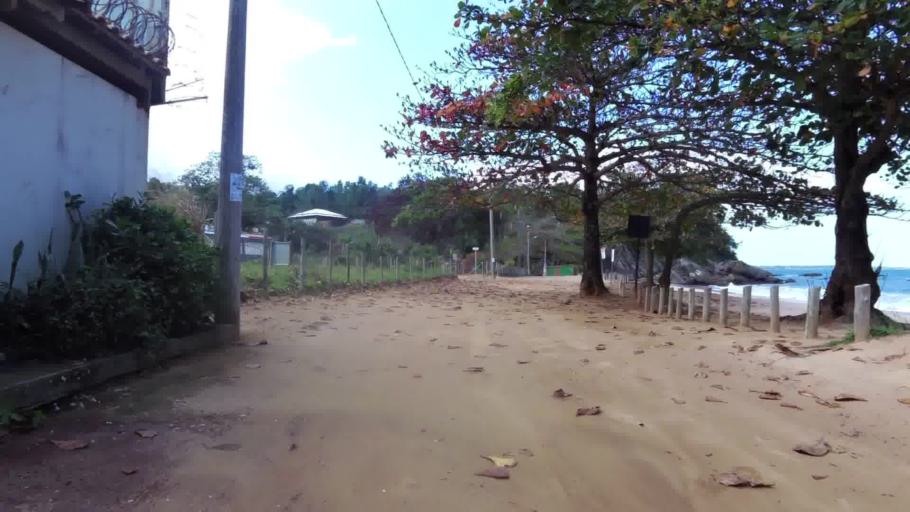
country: BR
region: Espirito Santo
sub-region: Piuma
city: Piuma
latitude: -20.8267
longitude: -40.6872
